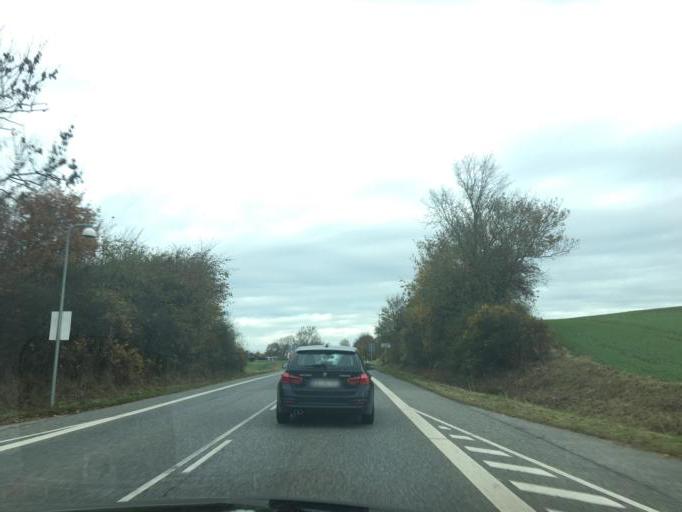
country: DK
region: South Denmark
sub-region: Vejle Kommune
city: Vejle
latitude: 55.6587
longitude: 9.5078
